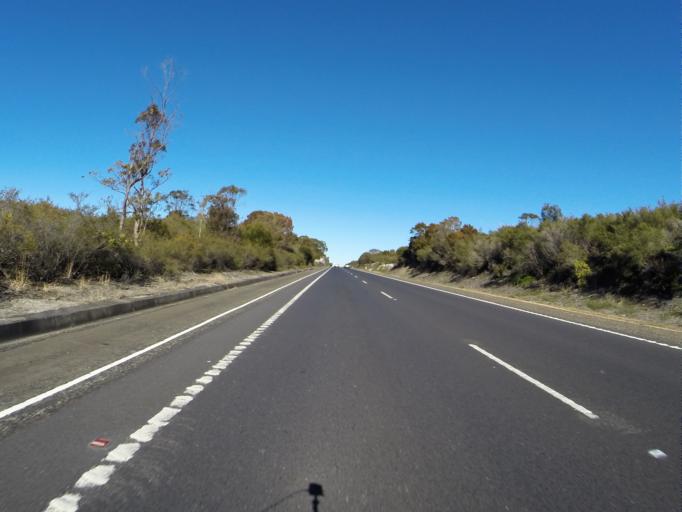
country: AU
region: New South Wales
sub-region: Wollongong
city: Bulli
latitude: -34.2542
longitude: 150.9332
